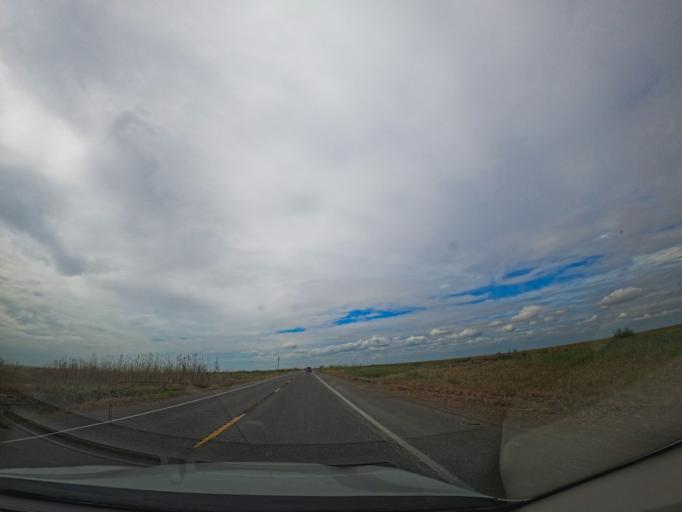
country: US
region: Louisiana
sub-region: Cameron Parish
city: Cameron
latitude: 29.7704
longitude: -93.4693
